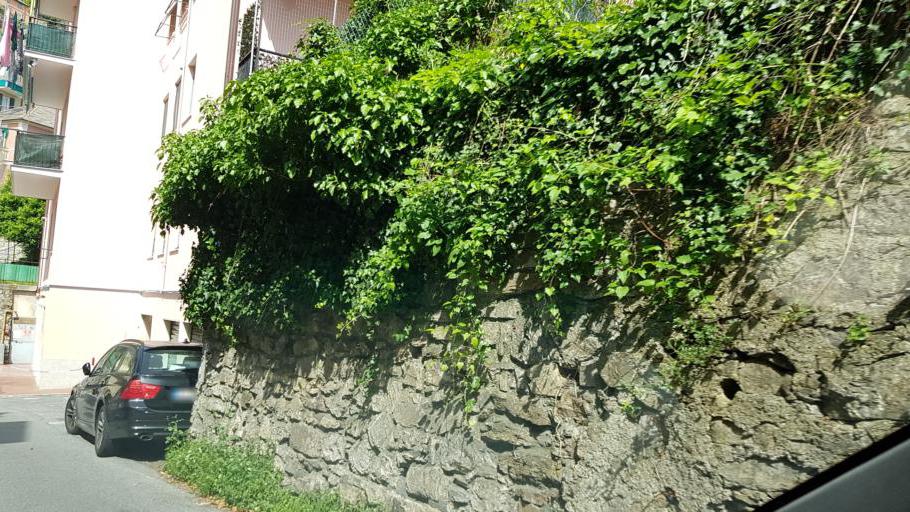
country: IT
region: Liguria
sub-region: Provincia di Genova
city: Genoa
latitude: 44.4043
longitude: 8.9904
